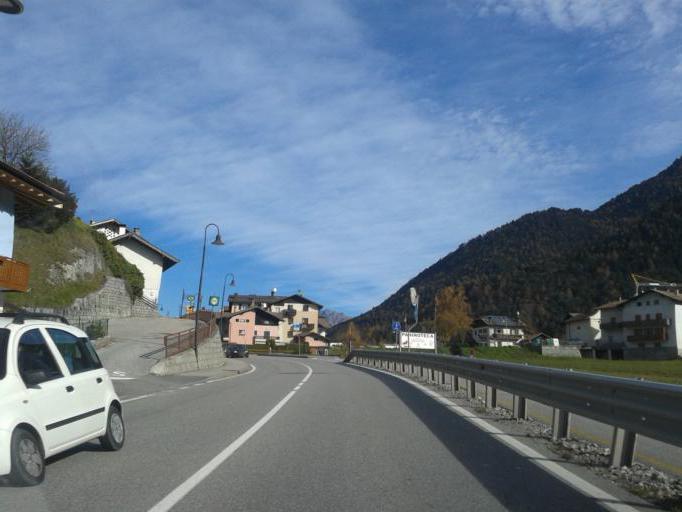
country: IT
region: Trentino-Alto Adige
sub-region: Provincia di Trento
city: Bondo
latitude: 45.9946
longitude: 10.6896
